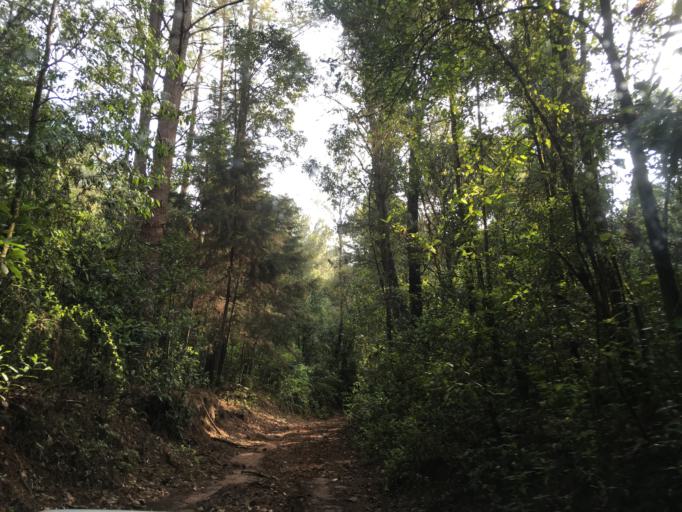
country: MX
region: Michoacan
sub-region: Zitacuaro
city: Francisco Serrato (San Bartolo)
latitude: 19.5082
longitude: -100.3041
